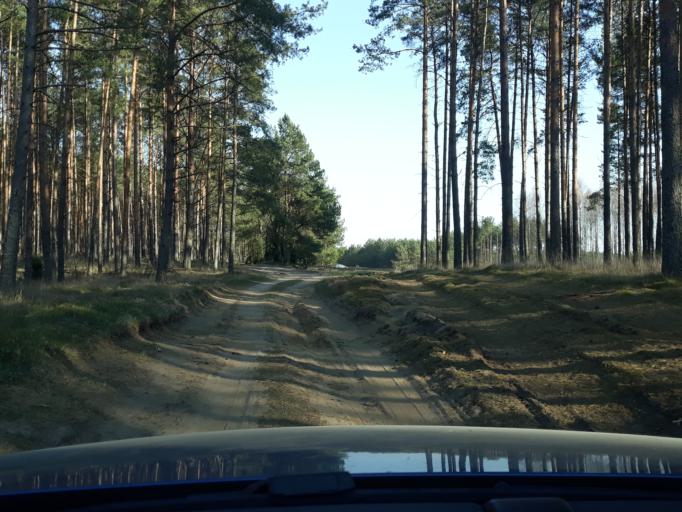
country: PL
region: Pomeranian Voivodeship
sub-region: Powiat bytowski
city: Lipnica
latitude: 53.9200
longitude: 17.4531
